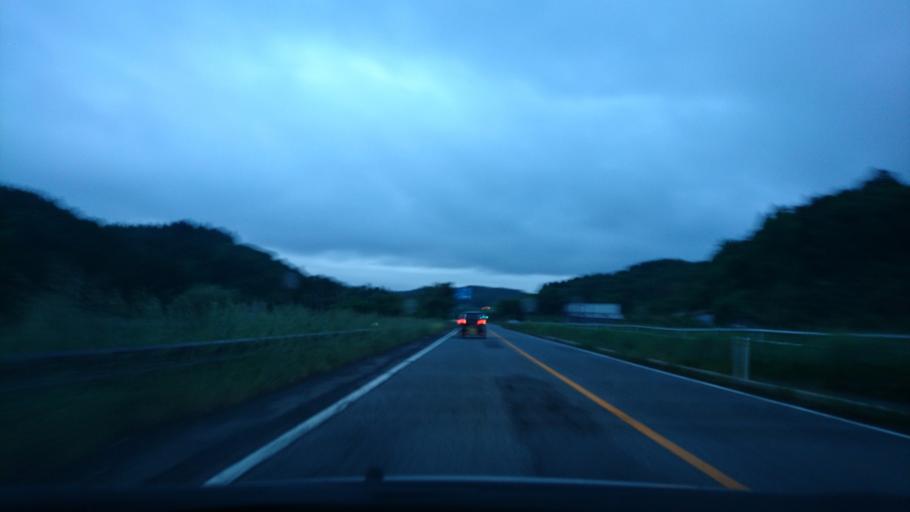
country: JP
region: Iwate
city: Ichinoseki
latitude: 38.8376
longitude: 141.0895
